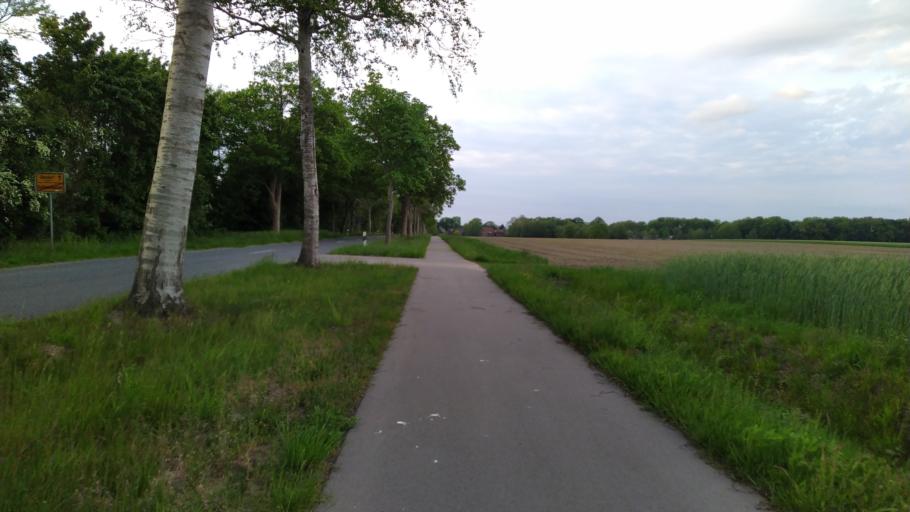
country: DE
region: Lower Saxony
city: Ahlerstedt
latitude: 53.3965
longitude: 9.4041
